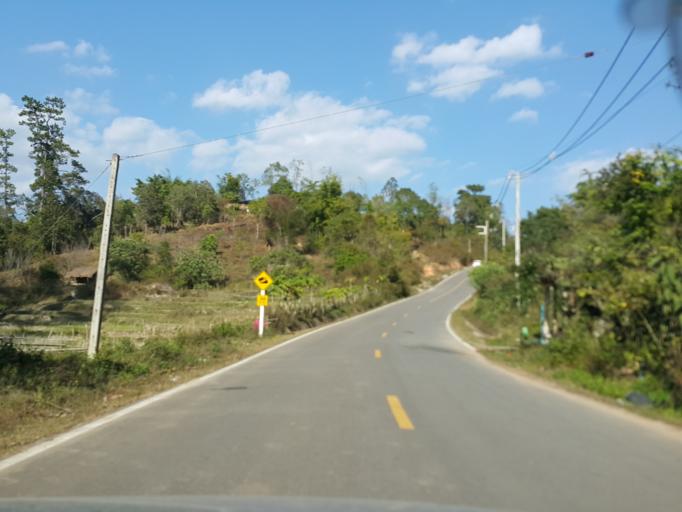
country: TH
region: Chiang Mai
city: Mae Wang
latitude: 18.6864
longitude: 98.5642
